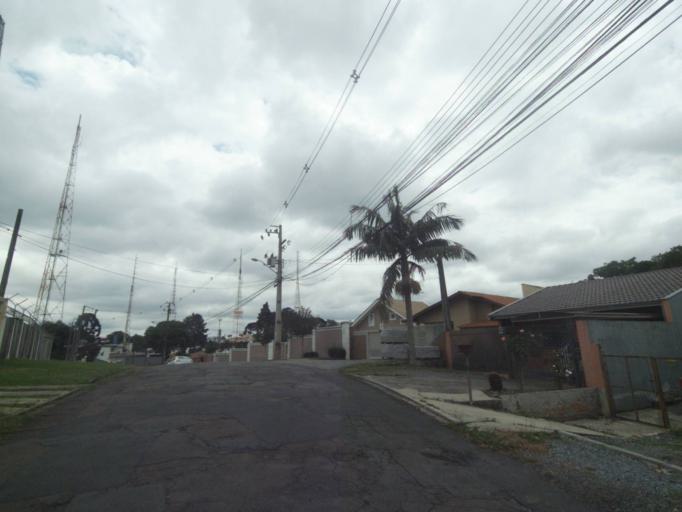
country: BR
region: Parana
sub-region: Curitiba
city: Curitiba
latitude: -25.3957
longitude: -49.2843
